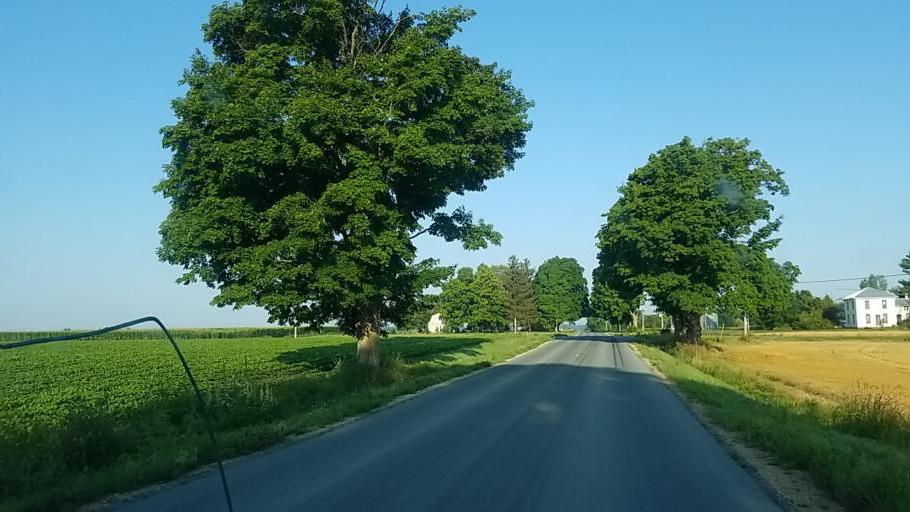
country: US
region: Michigan
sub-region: Montcalm County
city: Howard City
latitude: 43.3670
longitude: -85.4608
